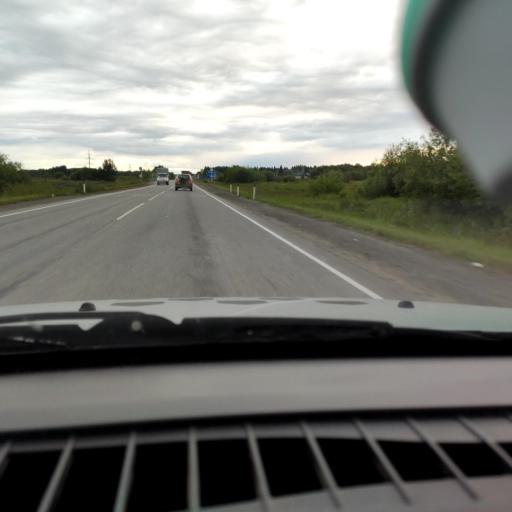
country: RU
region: Perm
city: Kalino
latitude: 58.3261
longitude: 57.6355
